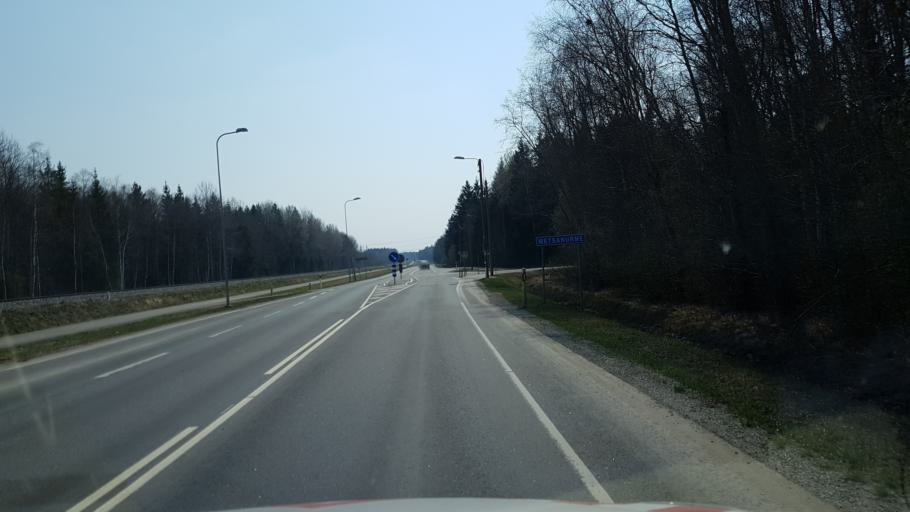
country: EE
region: Harju
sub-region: Saku vald
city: Saku
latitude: 59.2704
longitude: 24.6781
